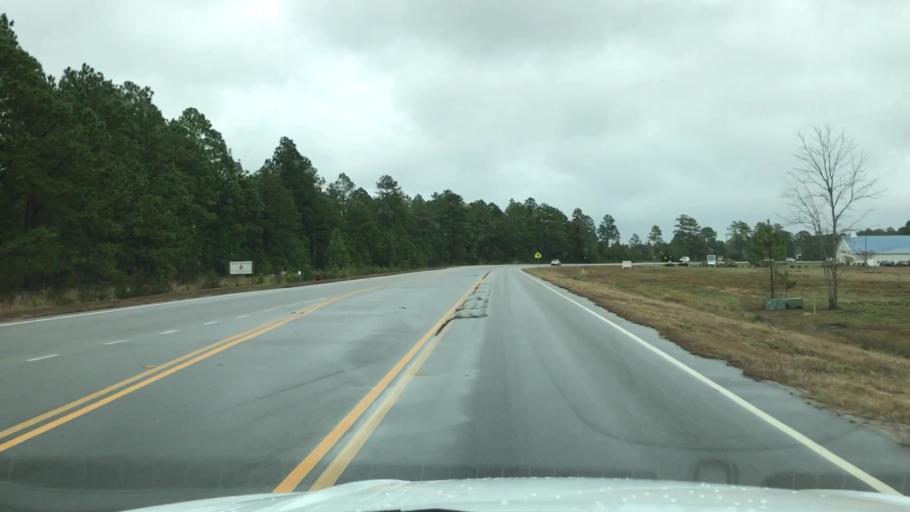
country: US
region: South Carolina
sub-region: Horry County
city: Myrtle Beach
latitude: 33.7612
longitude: -78.8903
